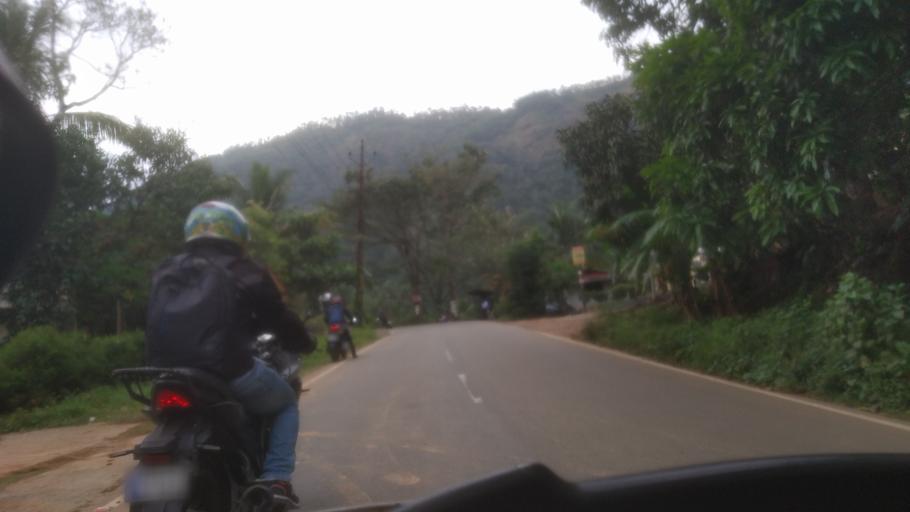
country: IN
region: Kerala
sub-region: Idukki
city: Munnar
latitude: 10.0000
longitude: 76.9688
